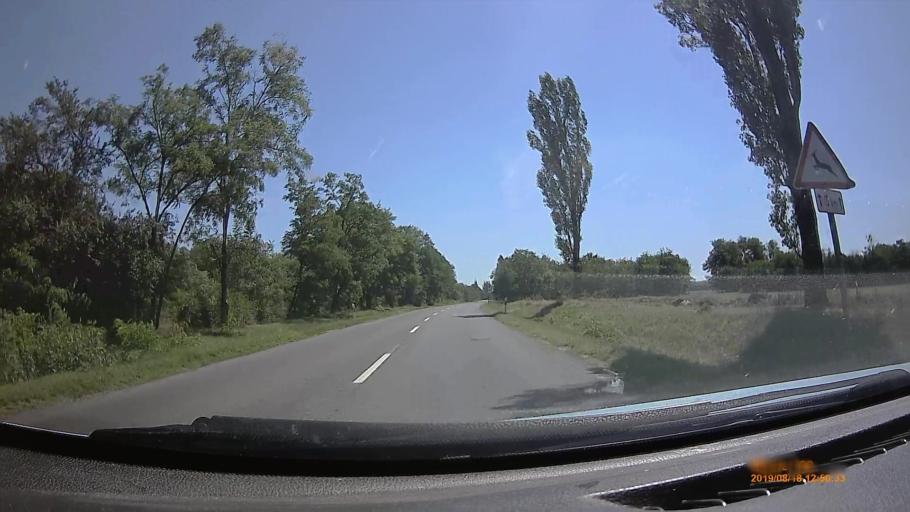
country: HU
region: Fejer
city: Aba
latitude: 47.0838
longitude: 18.4995
